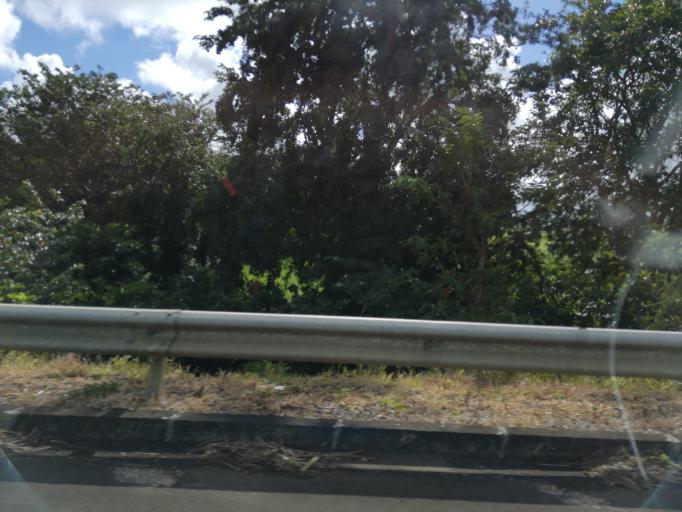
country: MU
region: Grand Port
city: Plaine Magnien
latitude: -20.4070
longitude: 57.6745
